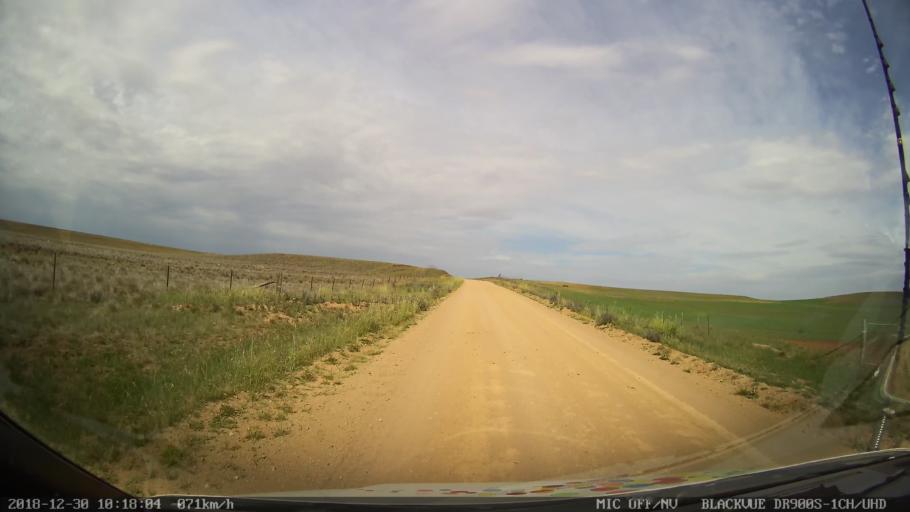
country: AU
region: New South Wales
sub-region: Snowy River
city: Berridale
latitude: -36.5505
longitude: 149.0132
